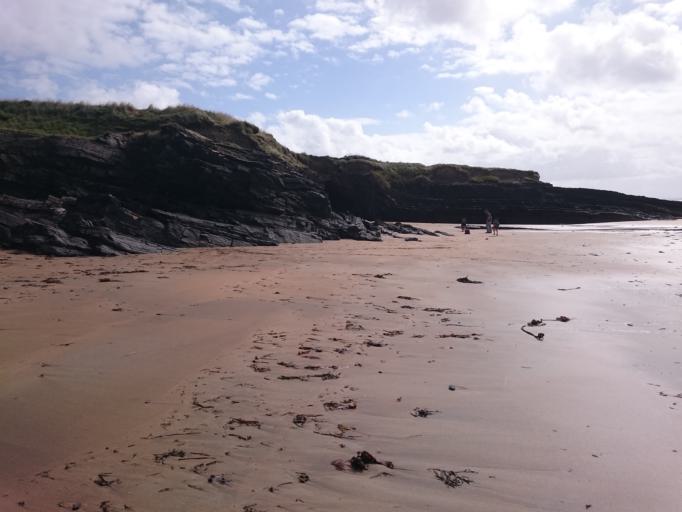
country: IE
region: Munster
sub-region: Ciarrai
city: Ballybunnion
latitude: 52.6157
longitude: -9.6504
